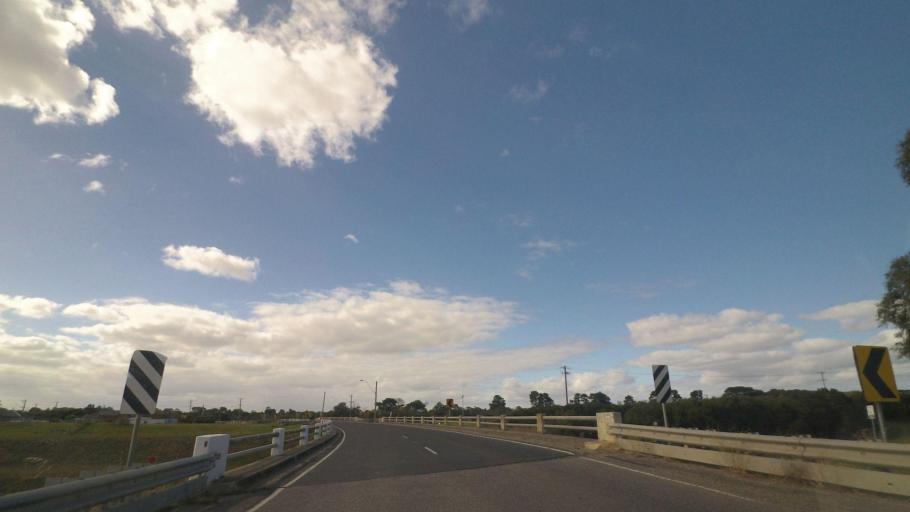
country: AU
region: Victoria
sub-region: Cardinia
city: Koo-Wee-Rup
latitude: -38.1963
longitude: 145.4770
